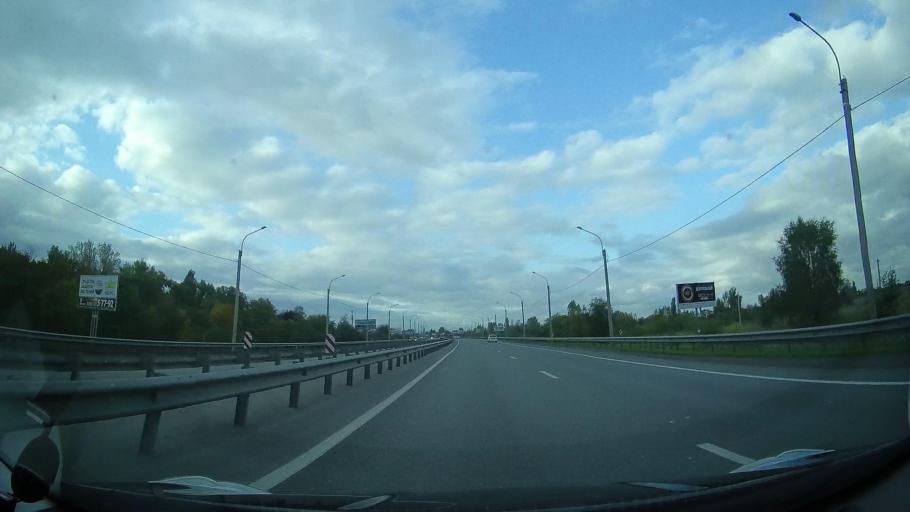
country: RU
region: Rostov
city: Bataysk
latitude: 47.1430
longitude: 39.7759
